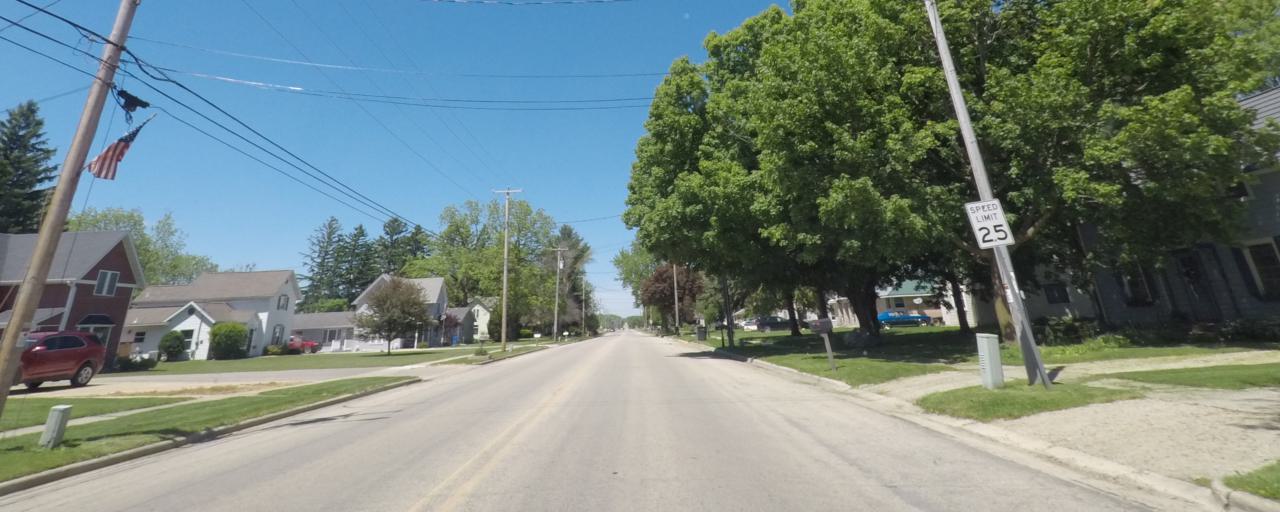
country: US
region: Wisconsin
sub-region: Green County
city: Brooklyn
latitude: 42.8551
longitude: -89.3691
